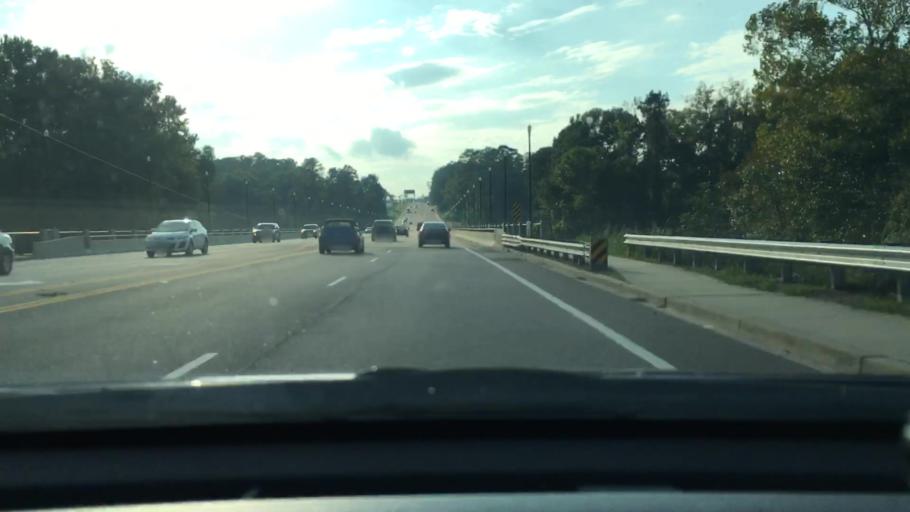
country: US
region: South Carolina
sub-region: Lexington County
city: West Columbia
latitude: 34.0265
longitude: -81.0667
